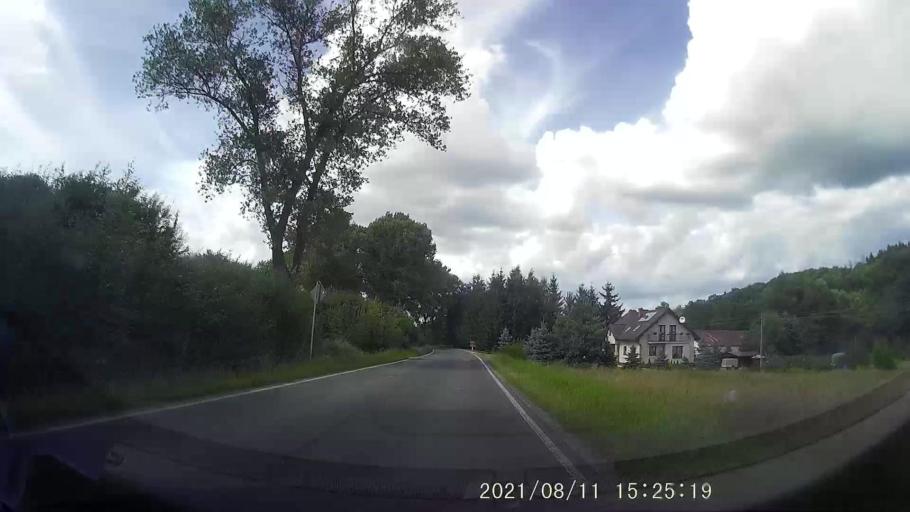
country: PL
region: Lower Silesian Voivodeship
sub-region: Powiat klodzki
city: Bystrzyca Klodzka
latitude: 50.2873
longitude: 16.6770
